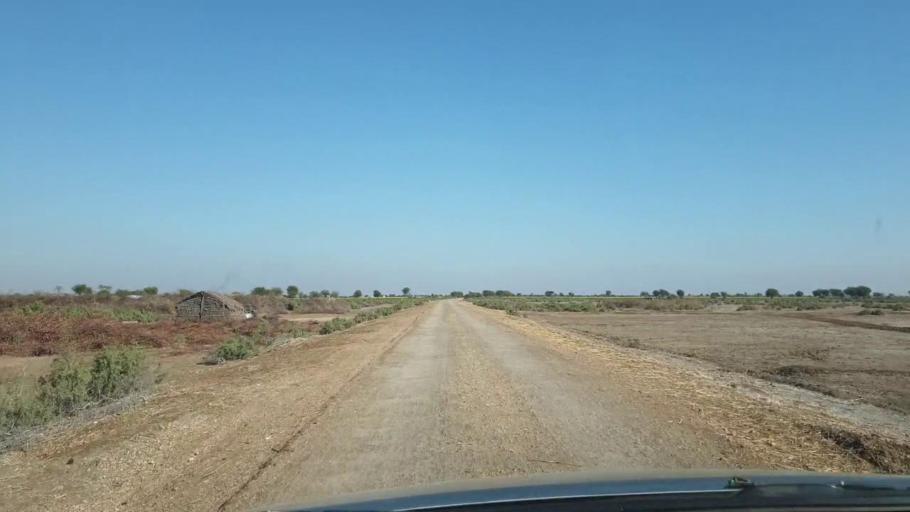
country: PK
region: Sindh
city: Jhol
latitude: 25.9163
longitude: 68.9757
